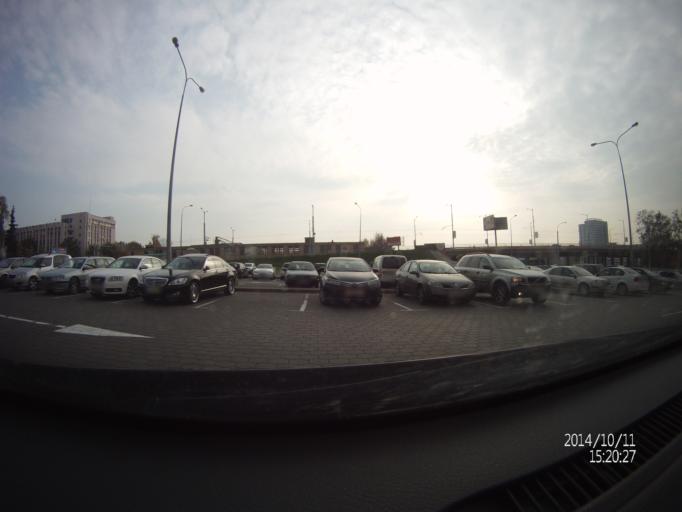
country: BY
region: Minsk
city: Minsk
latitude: 53.9074
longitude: 27.5275
